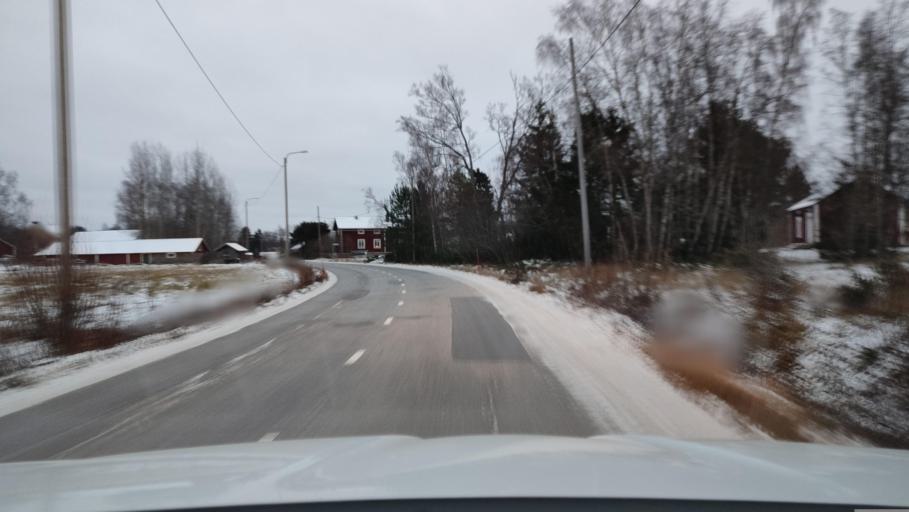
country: FI
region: Ostrobothnia
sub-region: Vaasa
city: Replot
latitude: 63.3477
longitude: 21.3051
